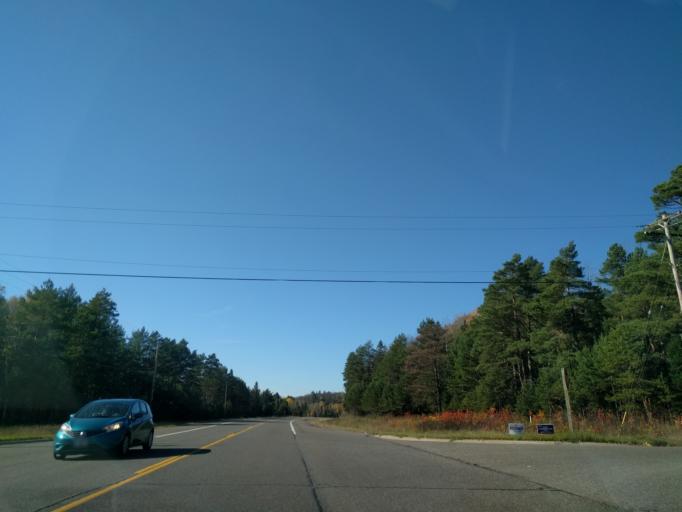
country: US
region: Michigan
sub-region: Marquette County
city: West Ishpeming
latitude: 46.4913
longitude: -87.8579
